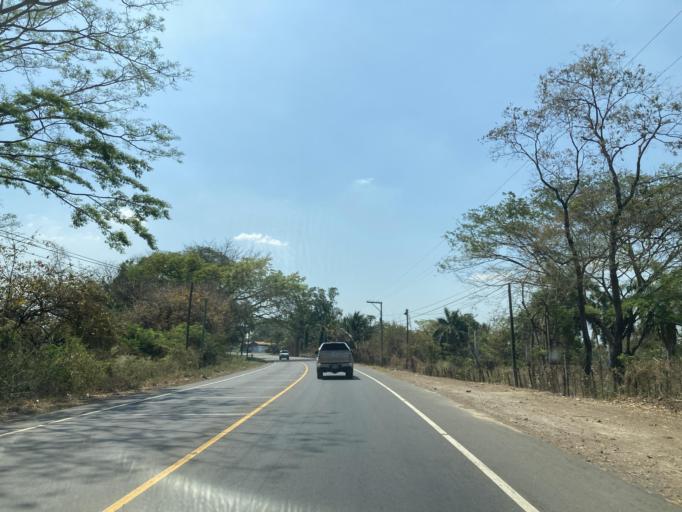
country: GT
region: Escuintla
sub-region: Municipio de Escuintla
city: Escuintla
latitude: 14.2393
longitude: -90.7420
